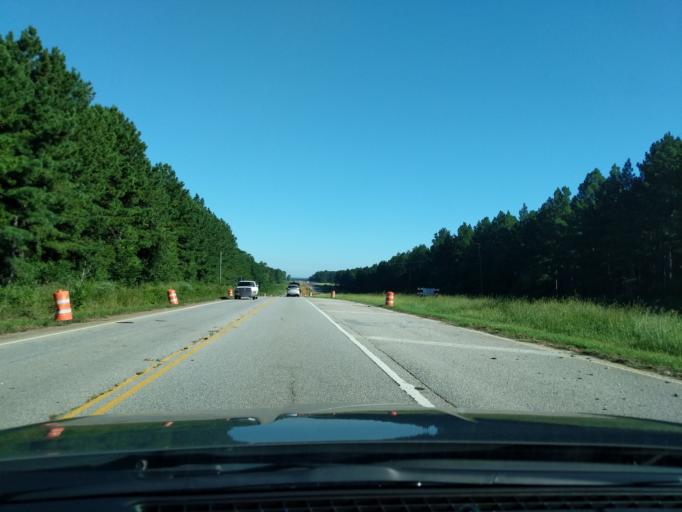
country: US
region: Georgia
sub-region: McDuffie County
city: Thomson
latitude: 33.5493
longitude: -82.5102
